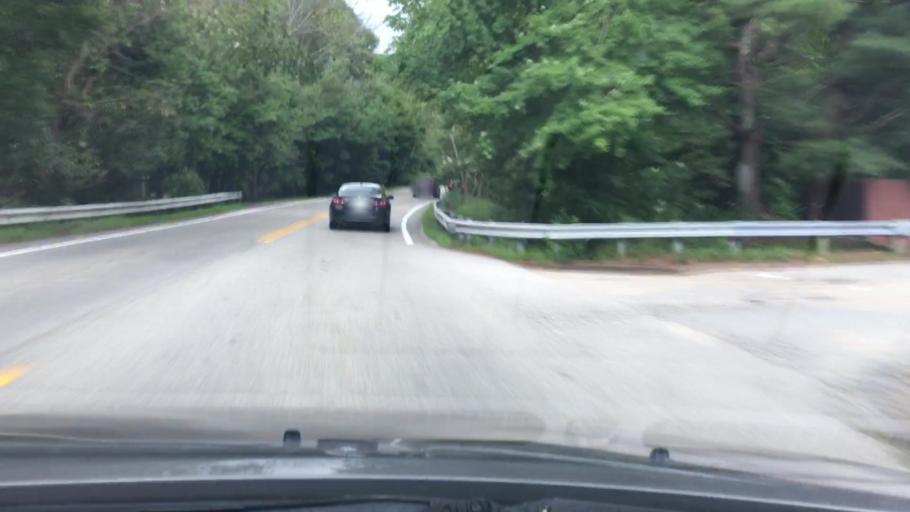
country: US
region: Rhode Island
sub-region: Providence County
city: Cumberland
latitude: 41.9966
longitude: -71.4167
